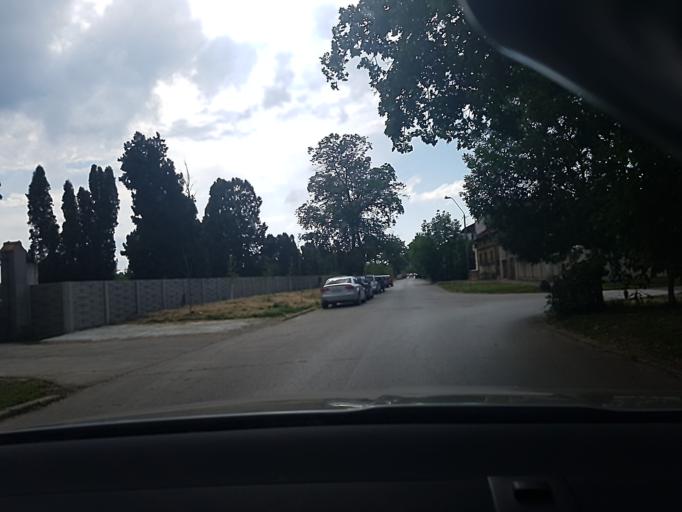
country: RO
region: Timis
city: Timisoara
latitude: 45.7379
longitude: 21.2222
